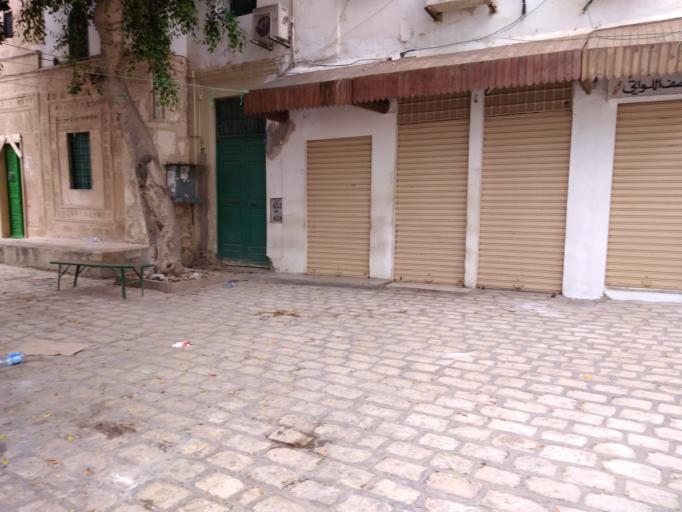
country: TN
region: Safaqis
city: Sfax
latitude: 34.7361
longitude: 10.7594
